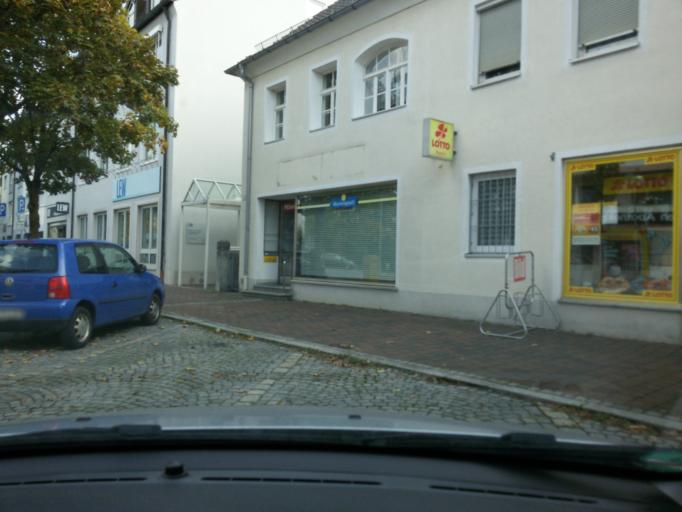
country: DE
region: Bavaria
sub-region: Swabia
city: Buchloe
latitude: 48.0357
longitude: 10.7230
